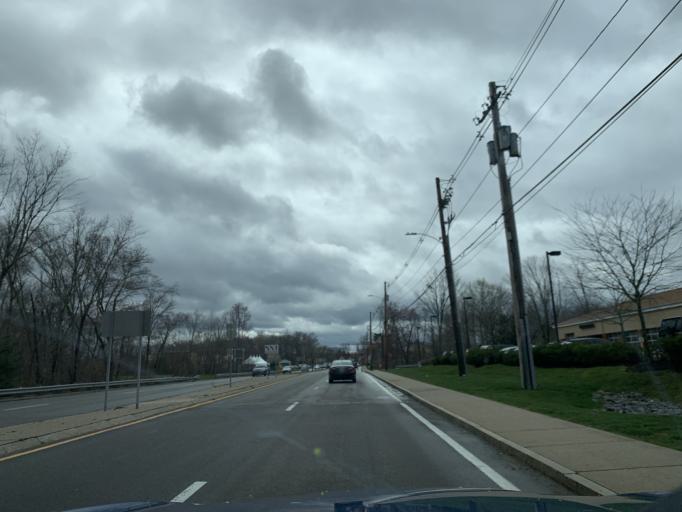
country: US
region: Massachusetts
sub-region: Bristol County
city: Mansfield Center
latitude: 42.0167
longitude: -71.2285
